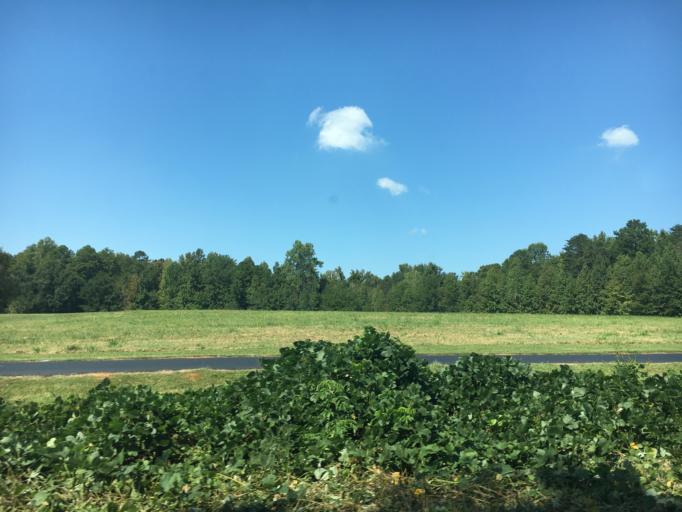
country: US
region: South Carolina
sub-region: Spartanburg County
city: Wellford
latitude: 34.8931
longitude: -82.1010
